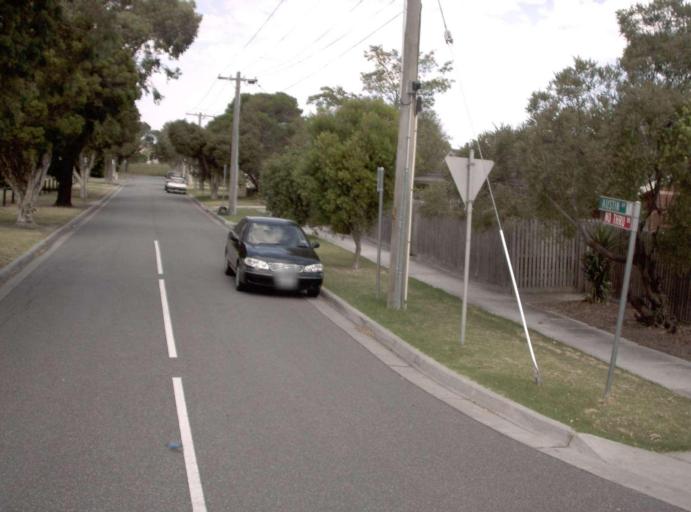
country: AU
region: Victoria
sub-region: Casey
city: Narre Warren
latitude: -38.0277
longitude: 145.3025
